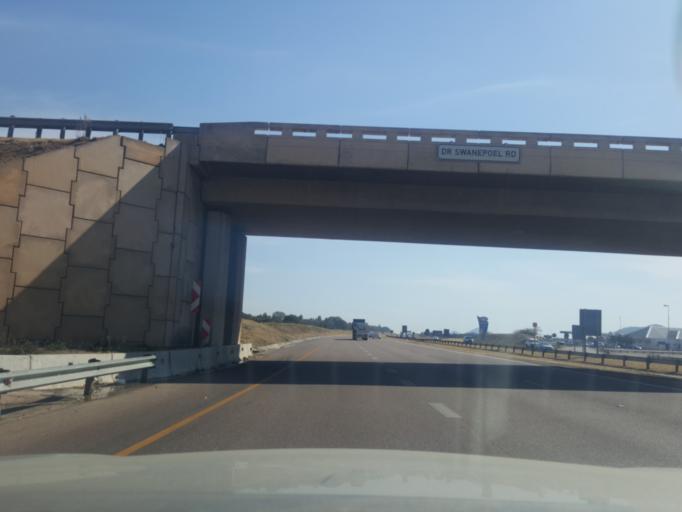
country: ZA
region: Gauteng
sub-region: City of Tshwane Metropolitan Municipality
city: Pretoria
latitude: -25.6437
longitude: 28.2458
